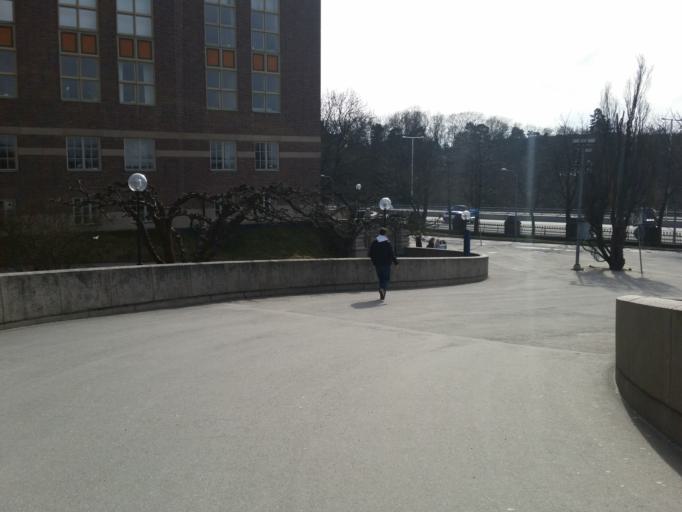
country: SE
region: Stockholm
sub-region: Norrtalje Kommun
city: Bergshamra
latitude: 59.3685
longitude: 18.0530
